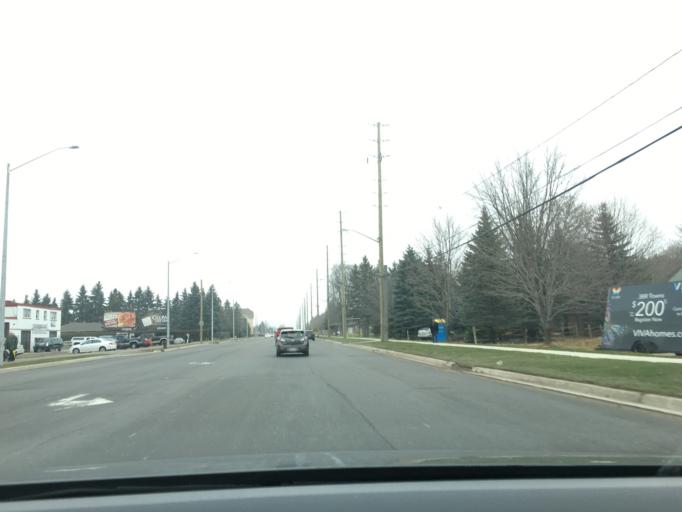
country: CA
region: Ontario
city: Innisfil
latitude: 44.3391
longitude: -79.7088
